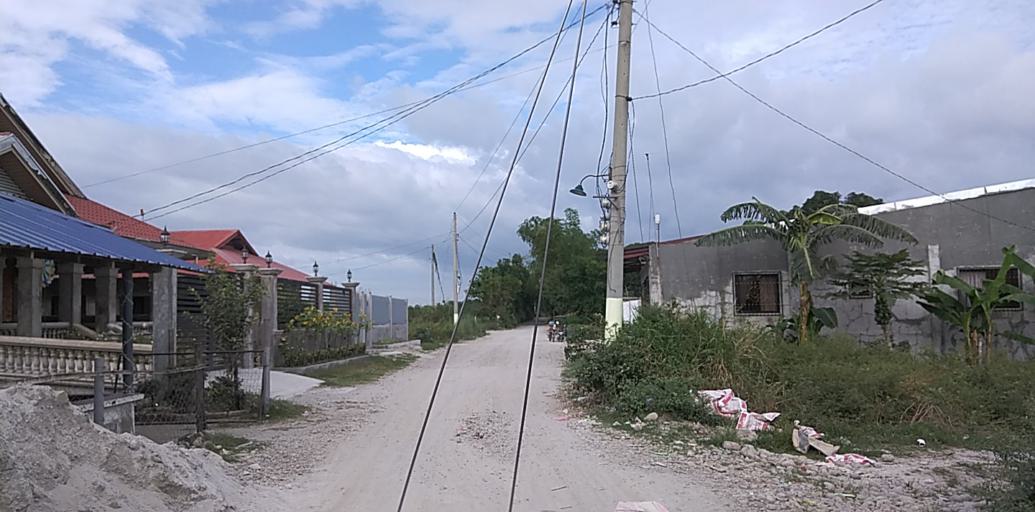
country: PH
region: Central Luzon
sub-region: Province of Pampanga
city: Pulung Santol
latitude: 15.0550
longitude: 120.5632
